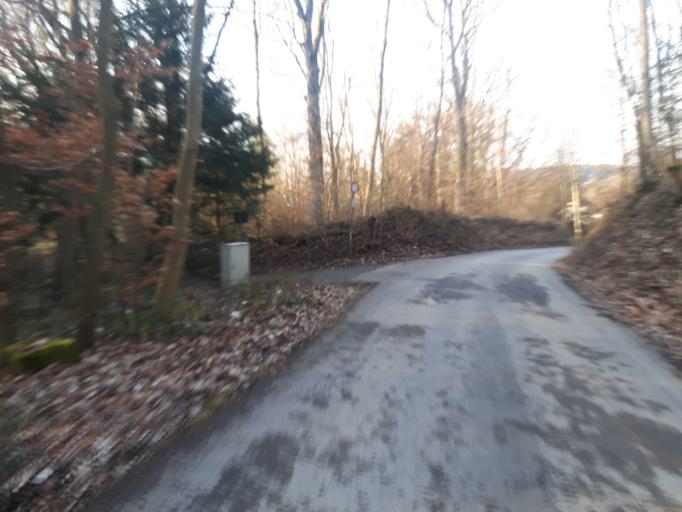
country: DE
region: Baden-Wuerttemberg
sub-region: Regierungsbezirk Stuttgart
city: Weinsberg
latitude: 49.1298
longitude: 9.2577
